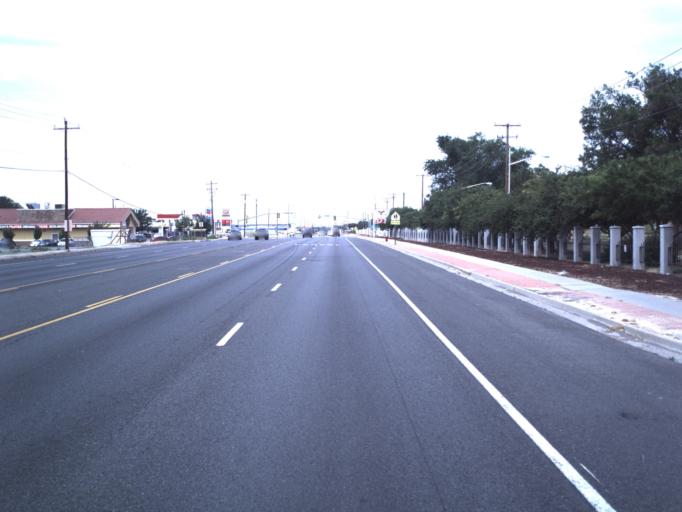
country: US
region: Utah
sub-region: Davis County
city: Clearfield
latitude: 41.0893
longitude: -112.0231
